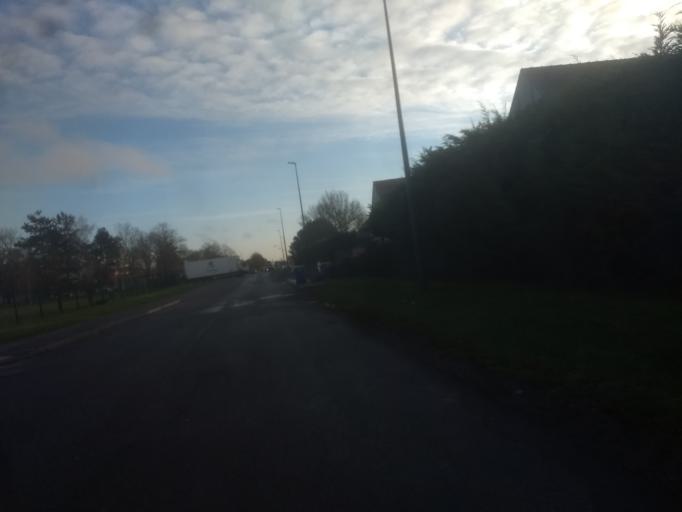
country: FR
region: Nord-Pas-de-Calais
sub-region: Departement du Pas-de-Calais
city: Dainville
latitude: 50.2921
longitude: 2.7263
